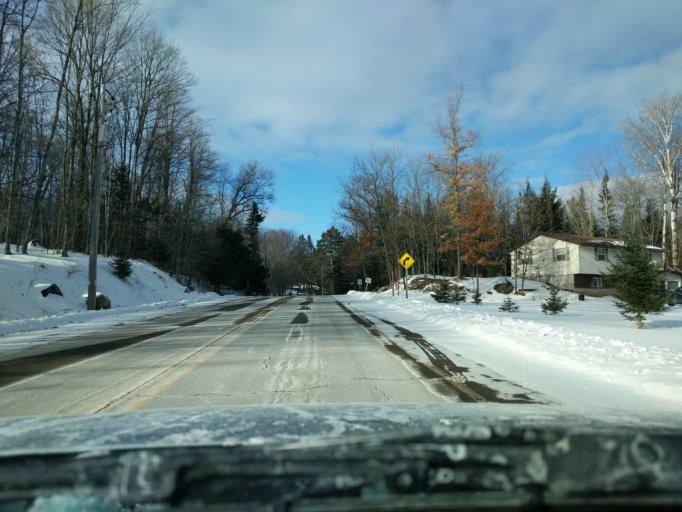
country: US
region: Wisconsin
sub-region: Vilas County
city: Eagle River
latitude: 45.7836
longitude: -89.0772
